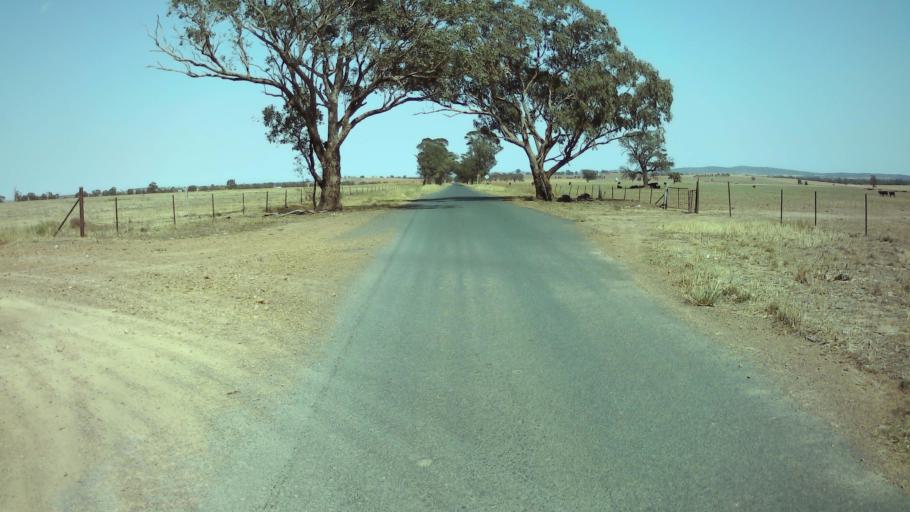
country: AU
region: New South Wales
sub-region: Weddin
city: Grenfell
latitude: -33.8592
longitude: 147.9716
